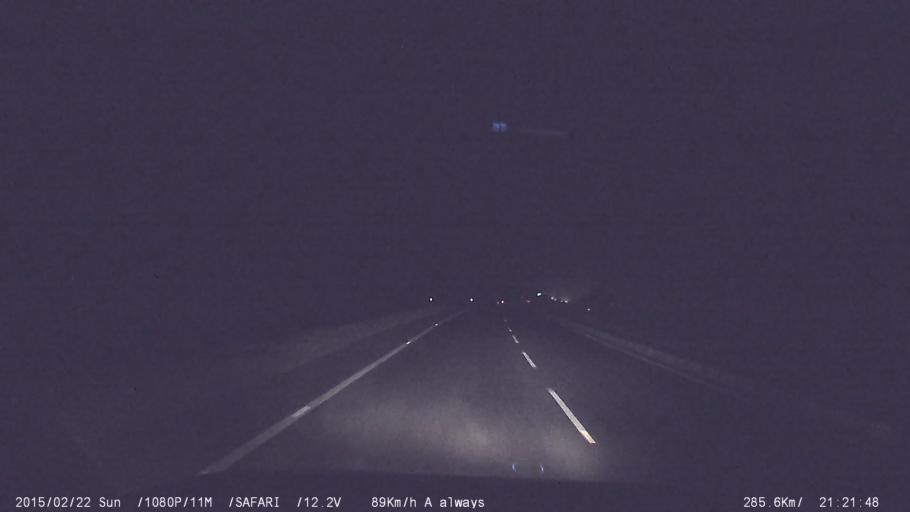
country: IN
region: Tamil Nadu
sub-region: Karur
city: Karur
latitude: 10.8675
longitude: 77.9940
